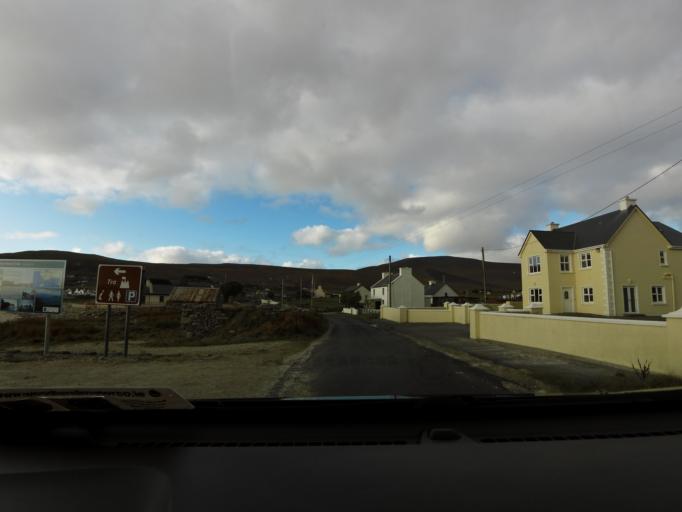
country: IE
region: Connaught
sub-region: Maigh Eo
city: Belmullet
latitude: 53.9212
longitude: -10.0182
